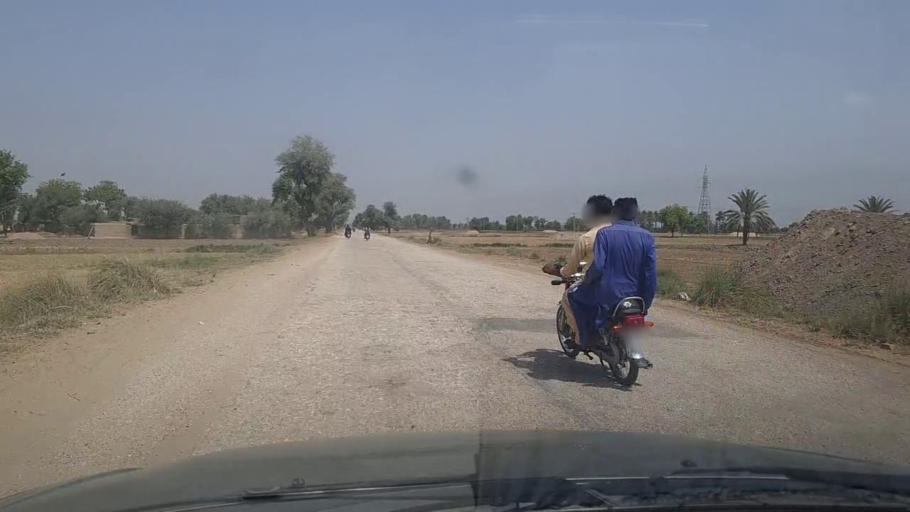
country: PK
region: Sindh
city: Setharja Old
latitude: 27.1502
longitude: 68.5235
